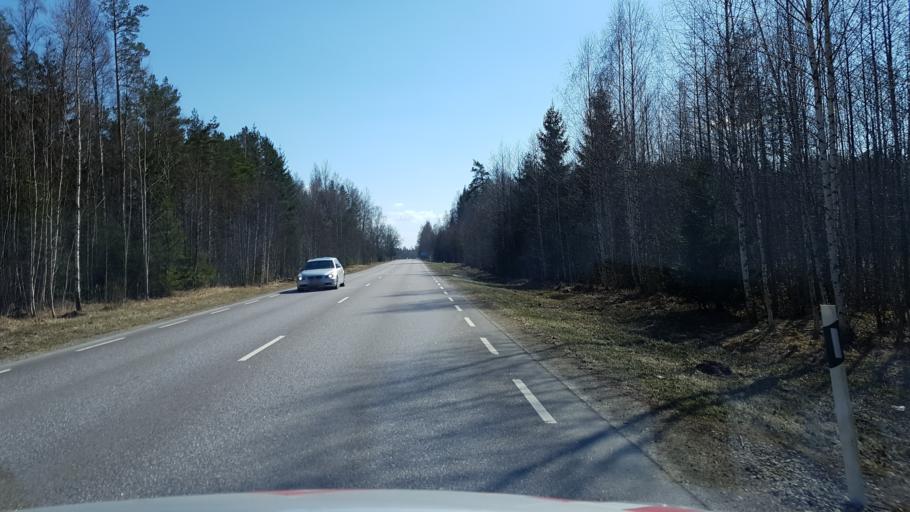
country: EE
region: Jogevamaa
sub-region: Tabivere vald
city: Tabivere
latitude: 58.6489
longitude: 26.7937
